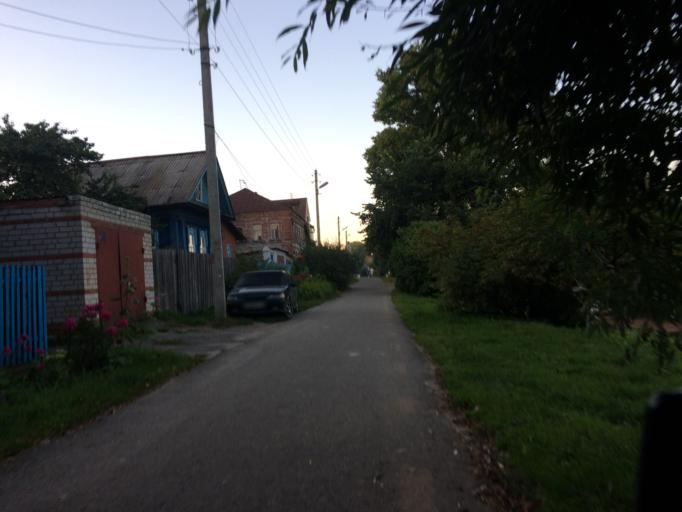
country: RU
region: Mariy-El
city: Yoshkar-Ola
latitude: 56.6398
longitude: 47.9052
